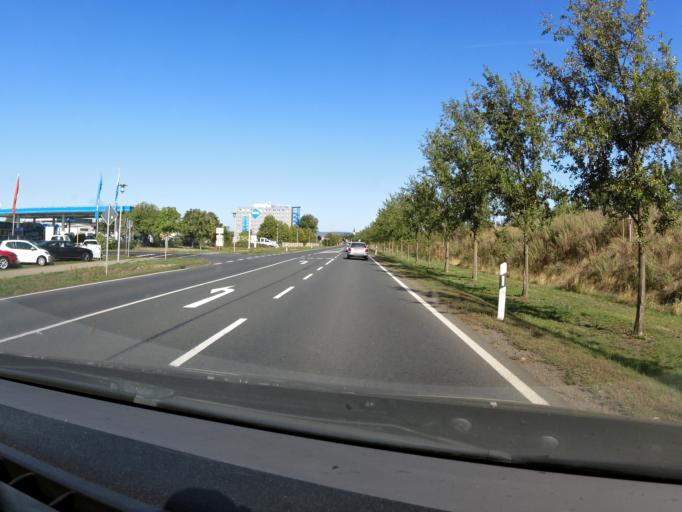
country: DE
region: Thuringia
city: Nordhausen
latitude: 51.4766
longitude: 10.8092
